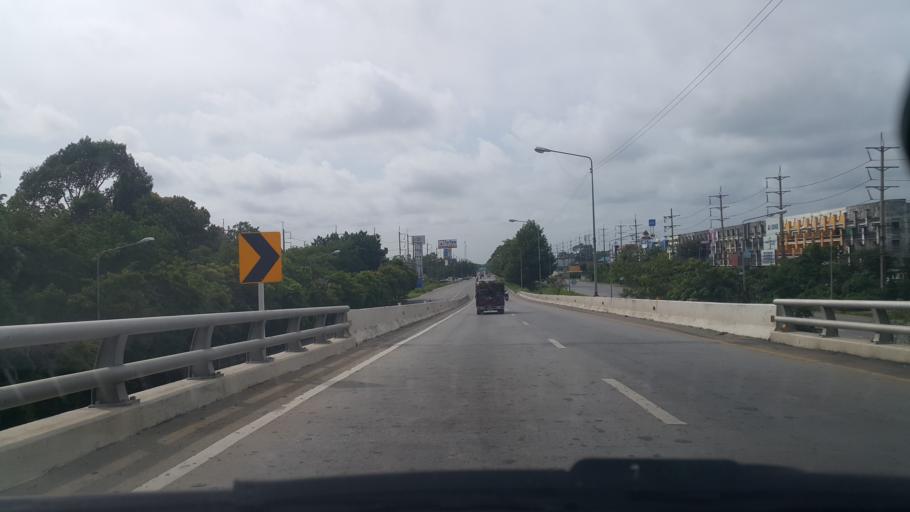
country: TH
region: Rayong
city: Rayong
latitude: 12.6637
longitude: 101.3090
